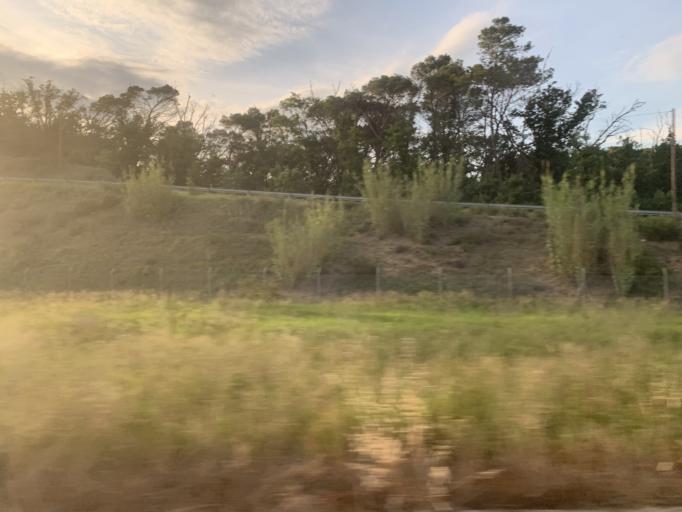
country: ES
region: Catalonia
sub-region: Provincia de Girona
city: Breda
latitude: 41.7338
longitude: 2.5961
